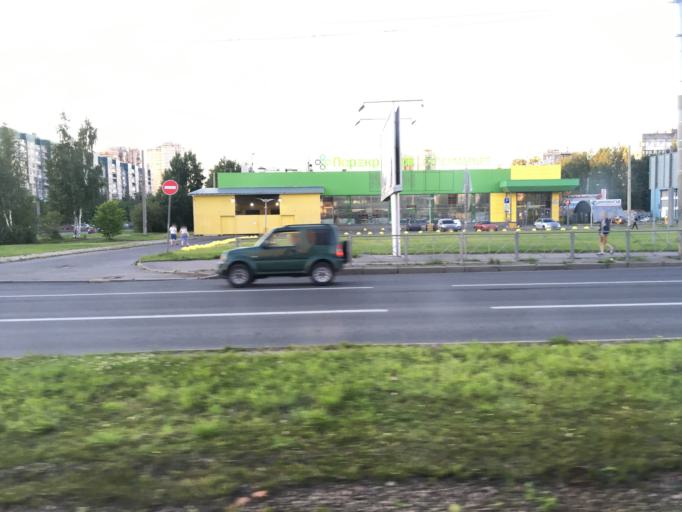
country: RU
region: St.-Petersburg
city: Komendantsky aerodrom
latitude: 60.0062
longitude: 30.2739
